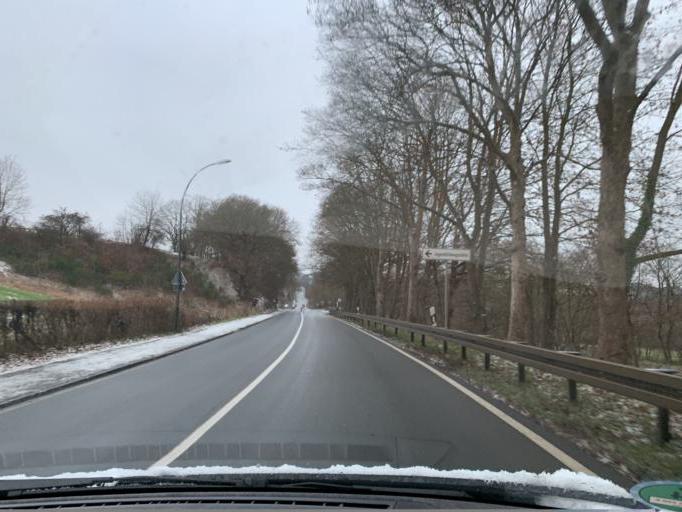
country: DE
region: North Rhine-Westphalia
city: Stolberg
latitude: 50.7377
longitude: 6.1755
